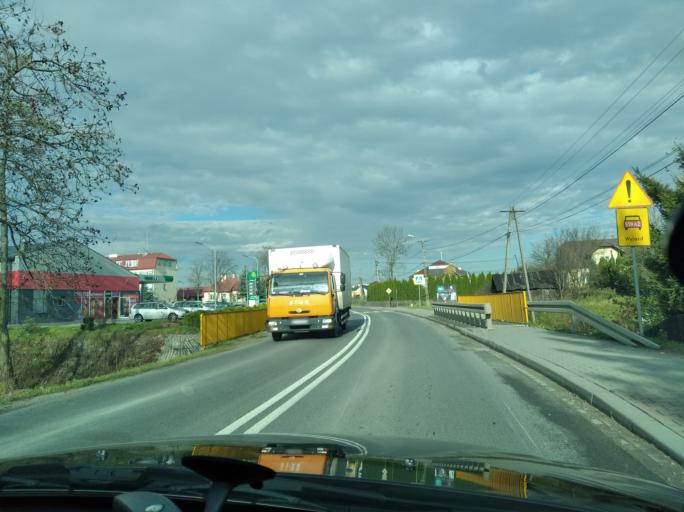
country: PL
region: Subcarpathian Voivodeship
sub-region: Powiat ropczycko-sedziszowski
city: Ostrow
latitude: 50.0973
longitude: 21.5937
